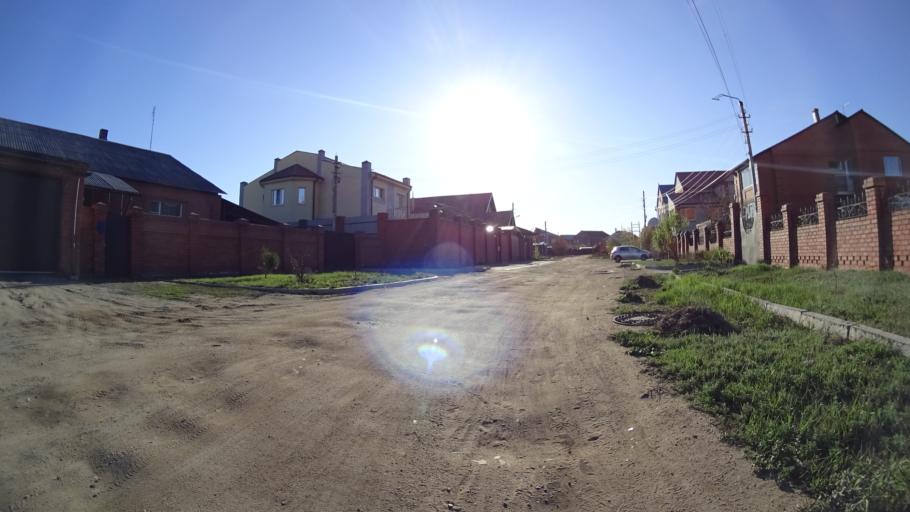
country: RU
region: Chelyabinsk
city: Troitsk
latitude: 54.0693
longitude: 61.5363
